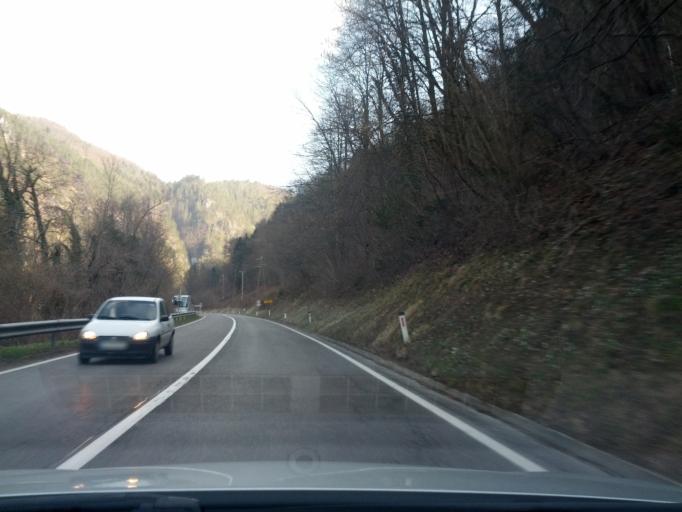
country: SI
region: Smartno pri Litiji
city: Smartno pri Litiji
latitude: 46.0886
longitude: 14.9027
